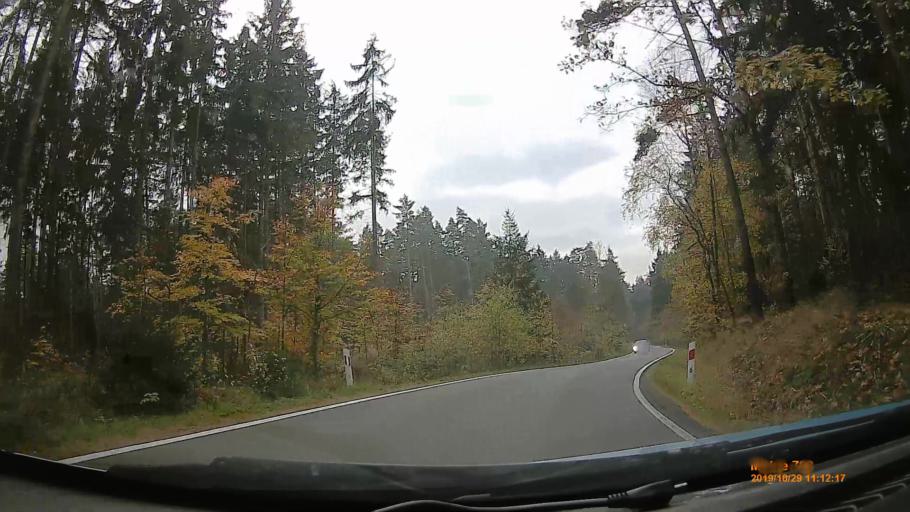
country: PL
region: Lower Silesian Voivodeship
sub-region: Powiat klodzki
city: Polanica-Zdroj
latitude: 50.4283
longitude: 16.5055
